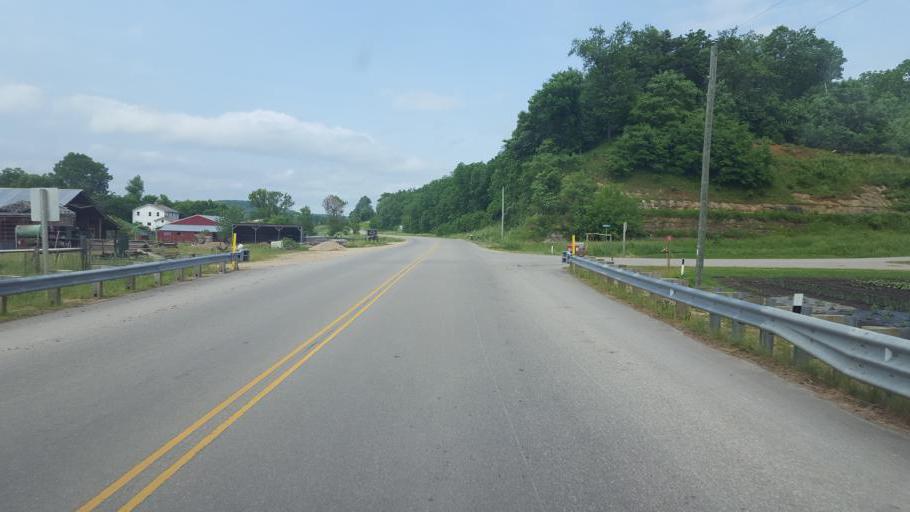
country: US
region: Wisconsin
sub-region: Monroe County
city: Cashton
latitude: 43.7294
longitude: -90.6343
